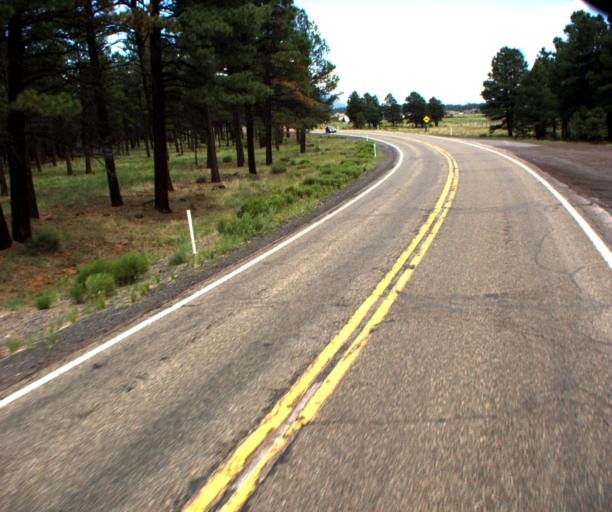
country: US
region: Arizona
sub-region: Coconino County
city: Flagstaff
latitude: 35.2683
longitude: -111.7404
